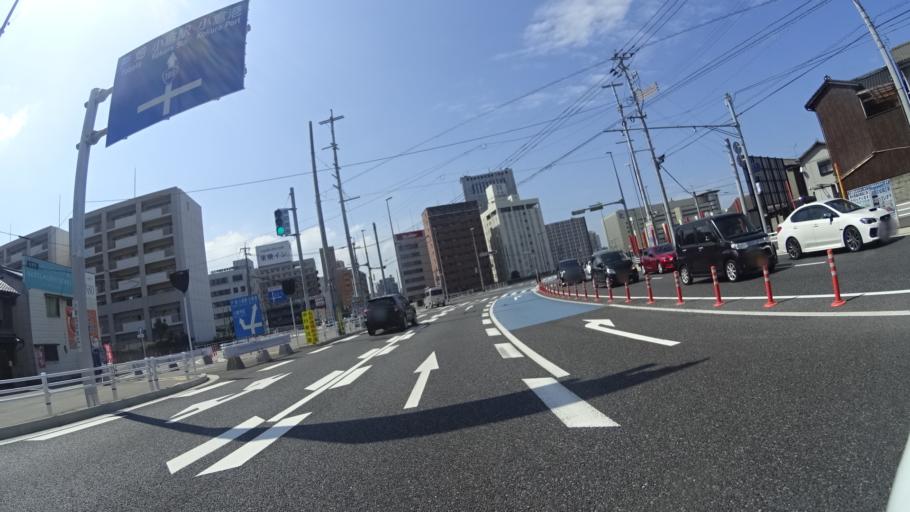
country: JP
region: Fukuoka
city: Kitakyushu
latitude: 33.8862
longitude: 130.8898
